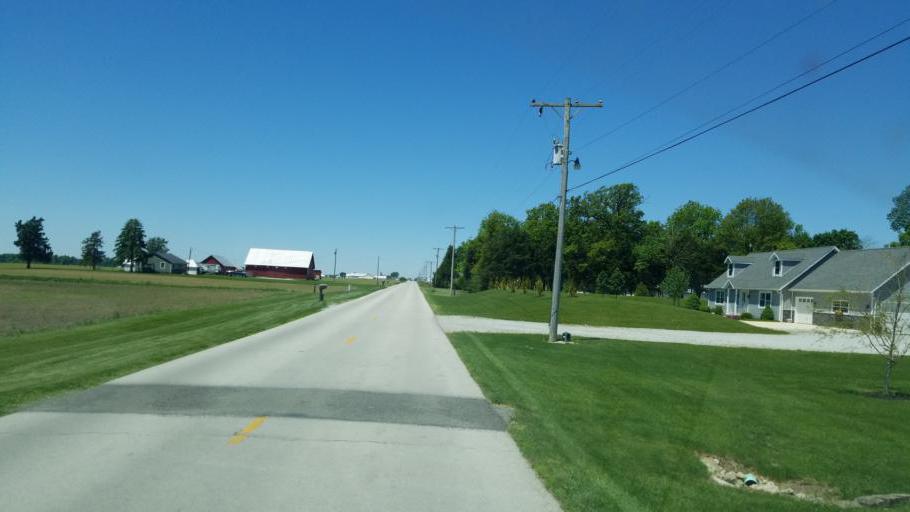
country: US
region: Ohio
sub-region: Auglaize County
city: Minster
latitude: 40.3856
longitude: -84.4136
